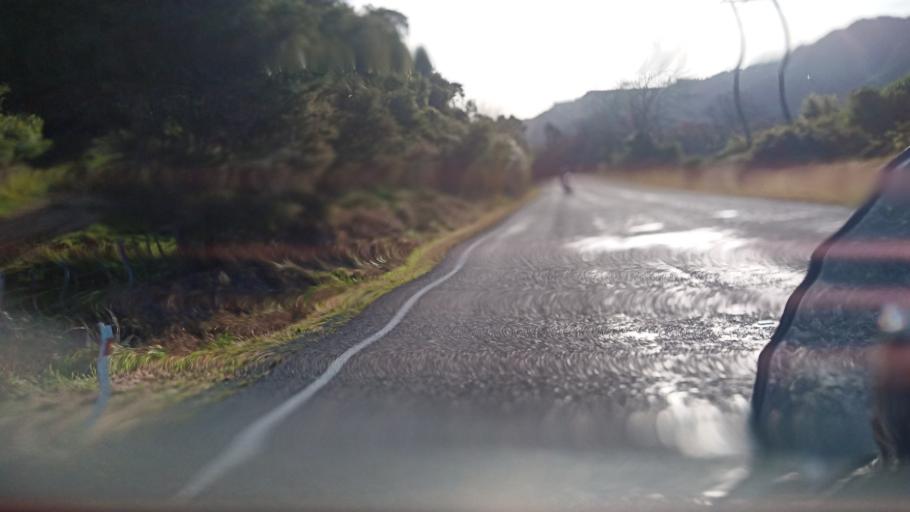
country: NZ
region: Gisborne
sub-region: Gisborne District
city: Gisborne
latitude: -38.4499
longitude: 177.6265
